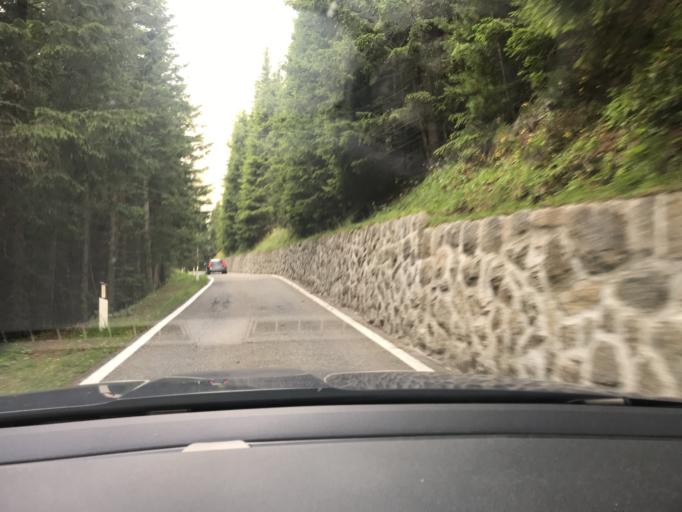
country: IT
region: Trentino-Alto Adige
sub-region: Bolzano
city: San Martino
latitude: 46.8905
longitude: 12.1926
